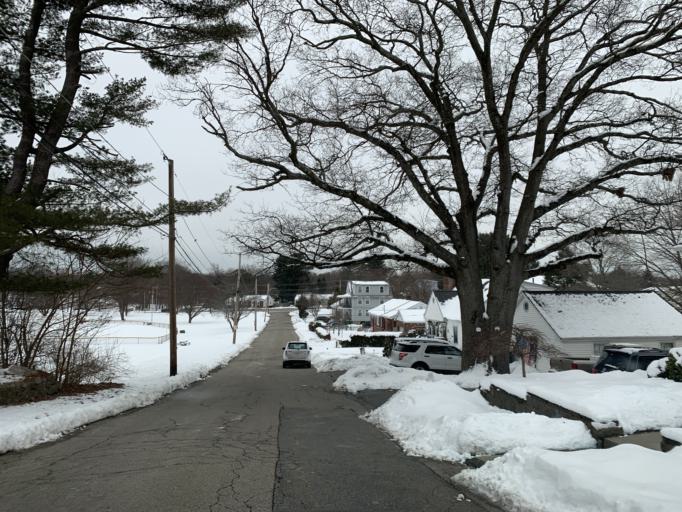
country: US
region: Massachusetts
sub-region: Norfolk County
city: Norwood
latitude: 42.1852
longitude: -71.1977
